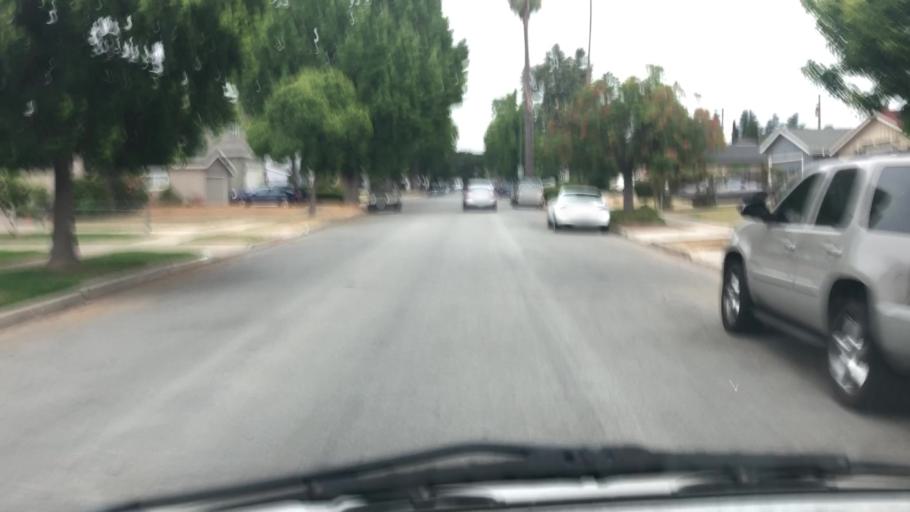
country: US
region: California
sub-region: Santa Clara County
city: Campbell
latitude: 37.3136
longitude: -121.9872
